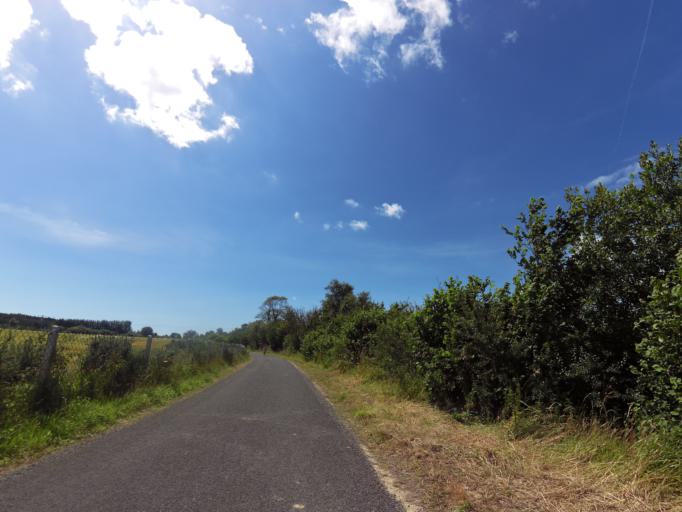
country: IE
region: Munster
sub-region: Waterford
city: Portlaw
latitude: 52.2377
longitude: -7.2983
